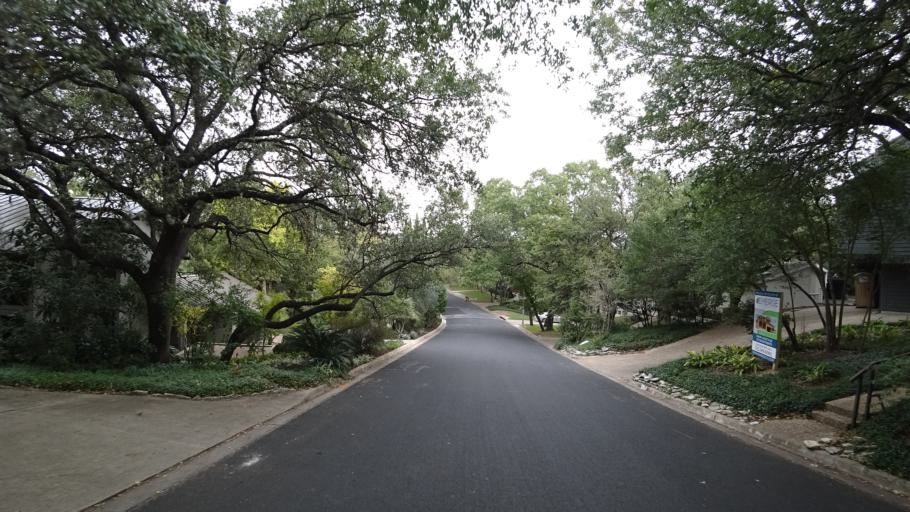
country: US
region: Texas
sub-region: Travis County
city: West Lake Hills
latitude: 30.3055
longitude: -97.7688
